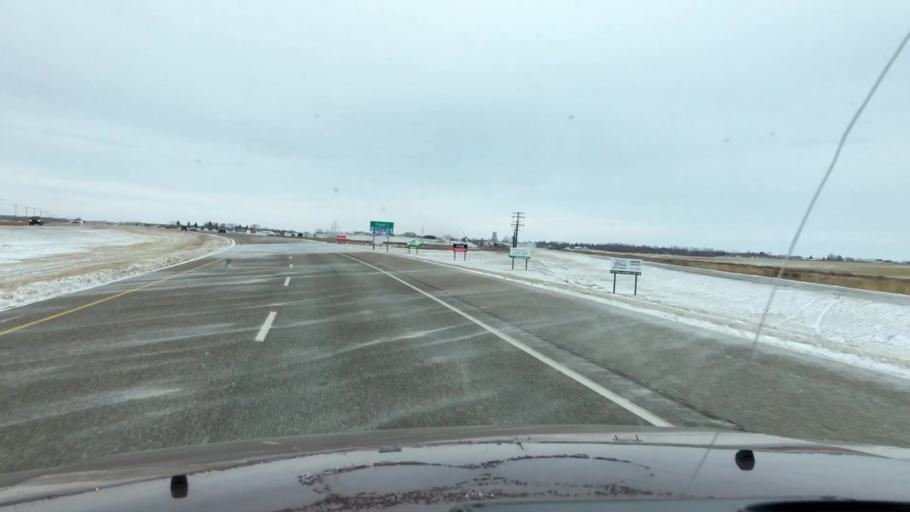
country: CA
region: Saskatchewan
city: Watrous
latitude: 51.0668
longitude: -105.8359
